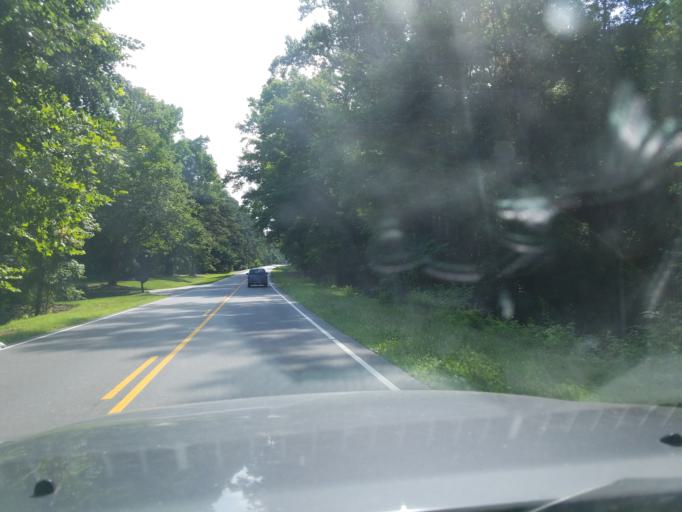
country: US
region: North Carolina
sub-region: Vance County
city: South Henderson
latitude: 36.3345
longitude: -78.4634
